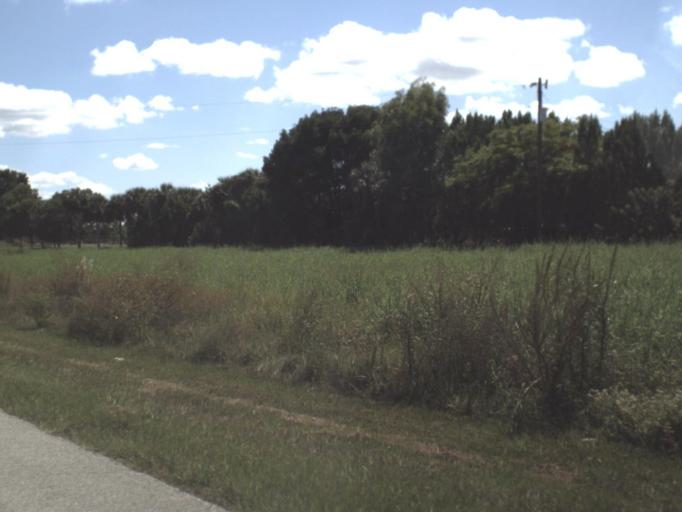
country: US
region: Florida
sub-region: Collier County
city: Lely Resort
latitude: 26.0190
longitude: -81.6300
